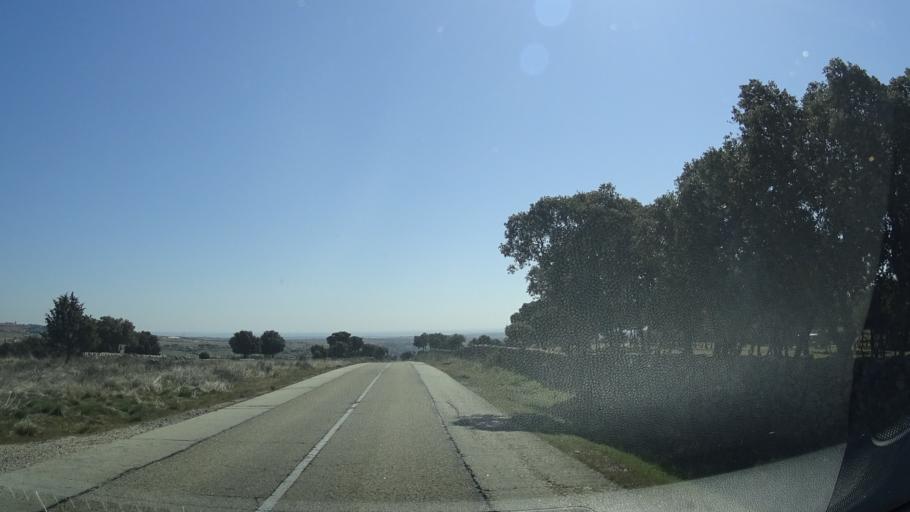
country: ES
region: Madrid
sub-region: Provincia de Madrid
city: Colmenar Viejo
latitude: 40.6456
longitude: -3.8228
